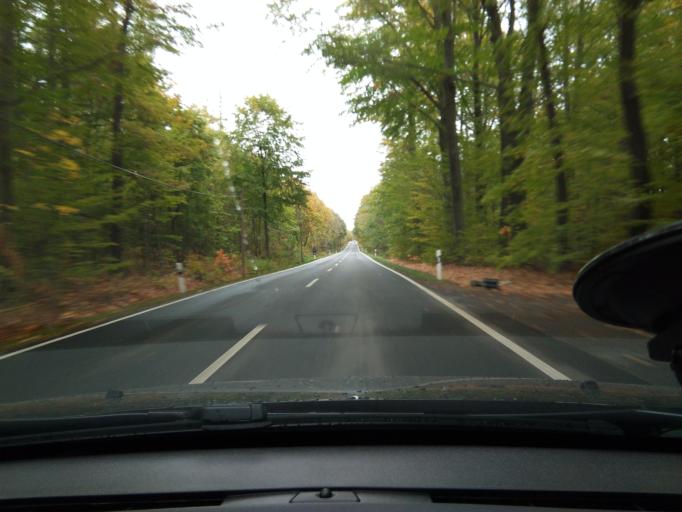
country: DE
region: Saxony
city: Moritzburg
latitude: 51.1609
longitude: 13.6560
